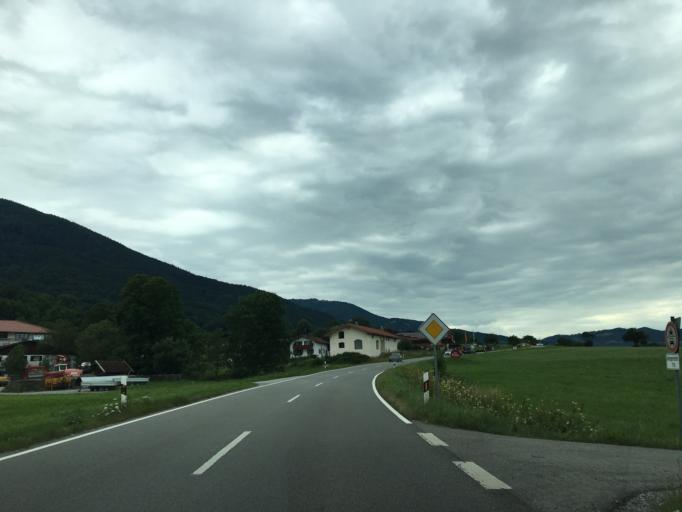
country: DE
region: Bavaria
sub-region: Upper Bavaria
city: Brannenburg
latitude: 47.7621
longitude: 12.0593
